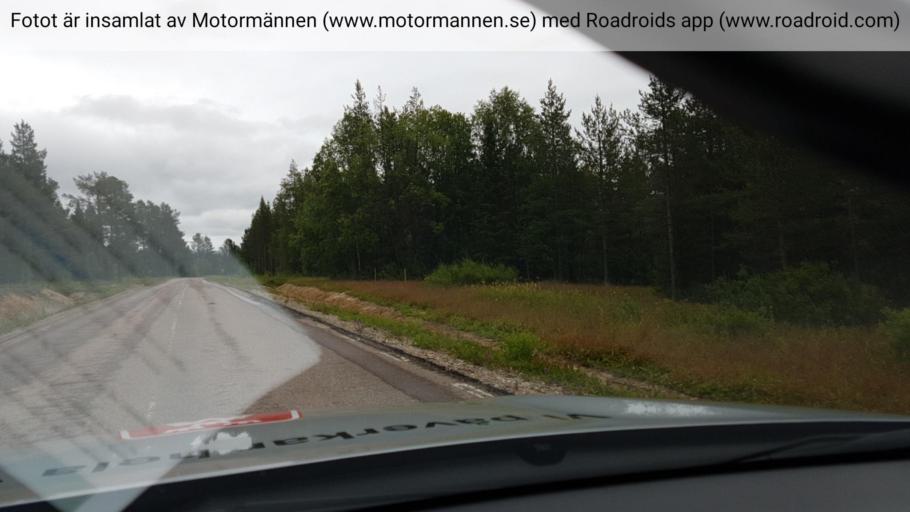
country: SE
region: Norrbotten
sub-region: Overkalix Kommun
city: OEverkalix
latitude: 67.0632
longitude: 22.2434
